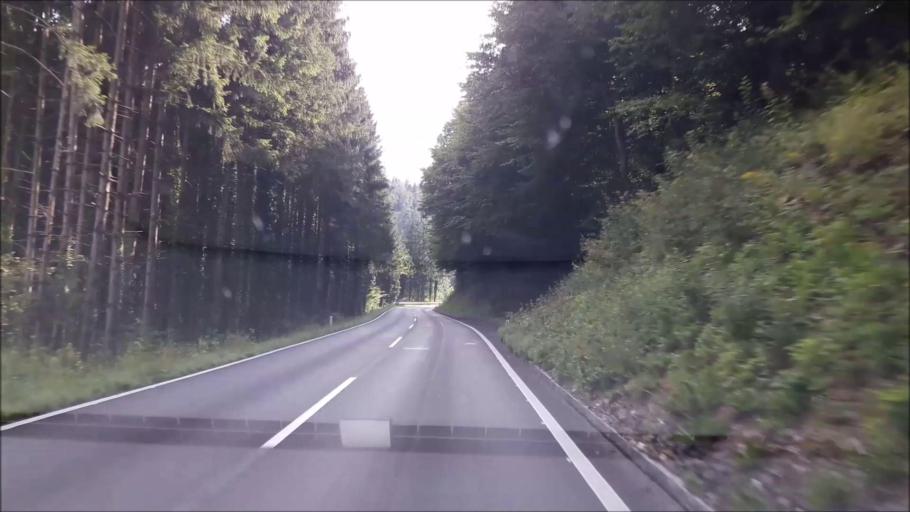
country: AT
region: Styria
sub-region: Politischer Bezirk Weiz
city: Floing
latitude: 47.2432
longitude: 15.7623
